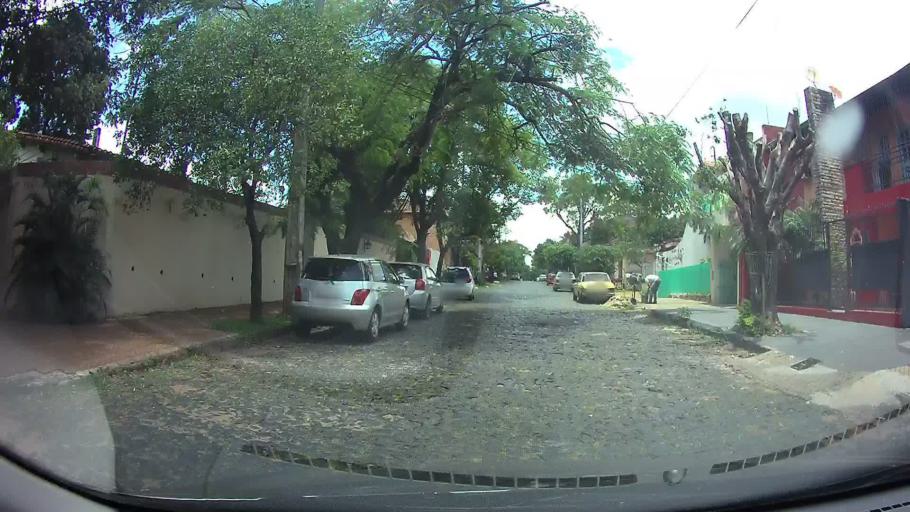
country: PY
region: Central
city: Lambare
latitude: -25.3122
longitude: -57.5937
